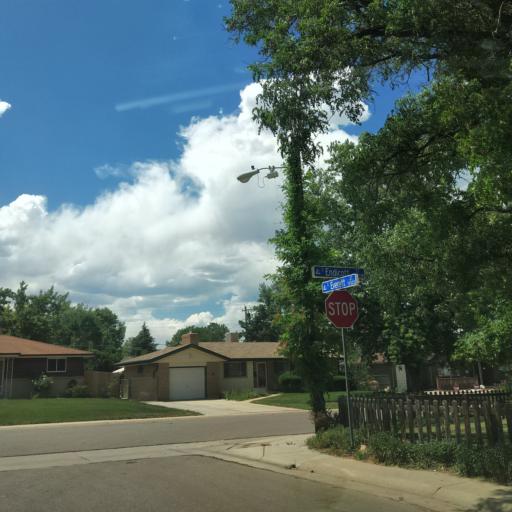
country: US
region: Colorado
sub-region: Jefferson County
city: Lakewood
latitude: 39.6886
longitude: -105.0973
